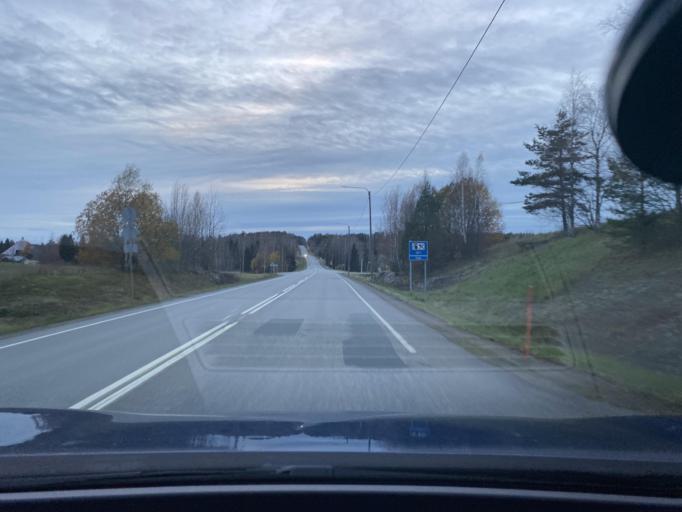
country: FI
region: Uusimaa
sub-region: Helsinki
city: Saukkola
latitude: 60.3855
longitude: 23.9979
